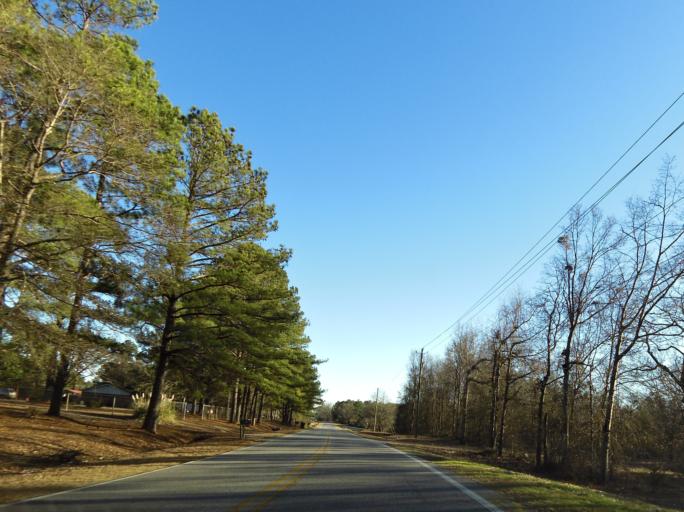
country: US
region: Georgia
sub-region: Peach County
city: Byron
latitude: 32.7066
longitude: -83.7099
